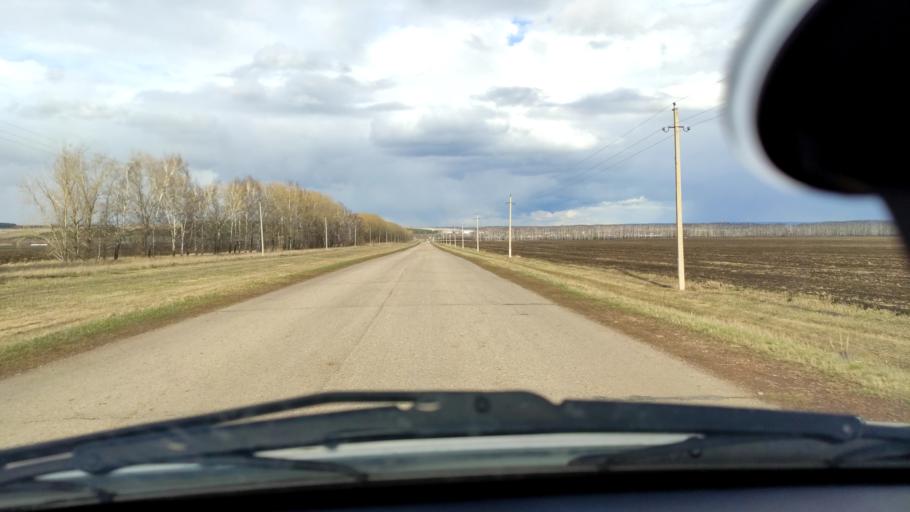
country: RU
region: Bashkortostan
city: Buzdyak
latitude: 54.7596
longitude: 54.5667
